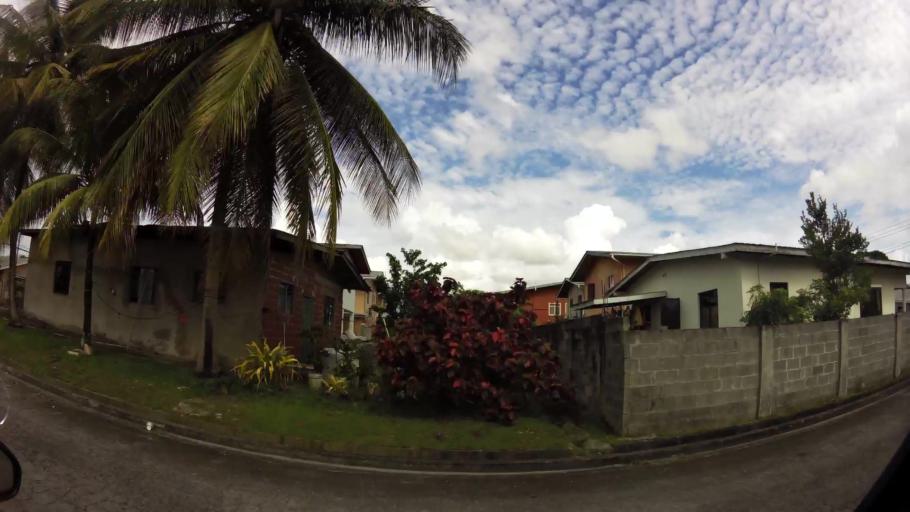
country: TT
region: Chaguanas
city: Chaguanas
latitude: 10.5097
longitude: -61.3930
